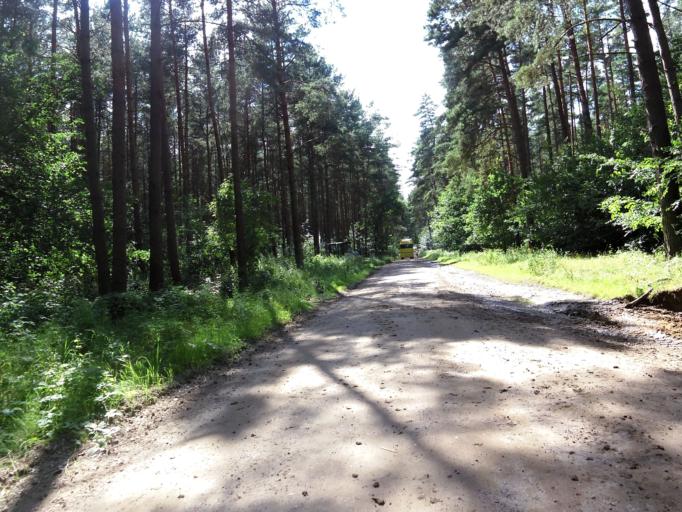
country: DE
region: Brandenburg
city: Lychen
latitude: 53.2945
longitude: 13.3563
